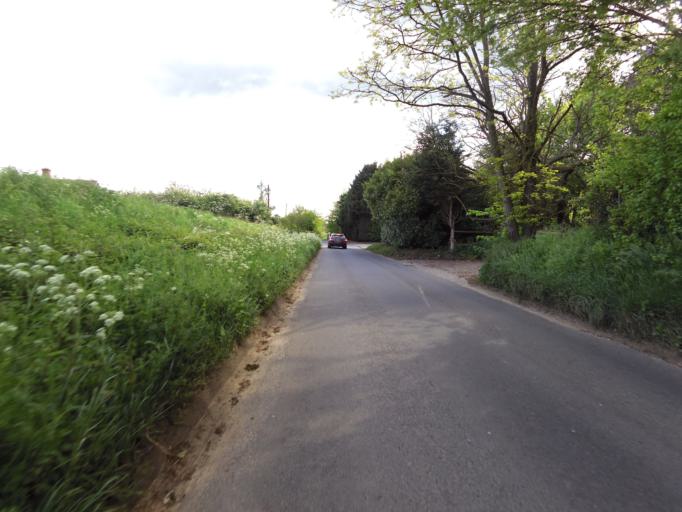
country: GB
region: England
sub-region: Suffolk
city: Stowmarket
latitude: 52.1931
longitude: 0.9659
